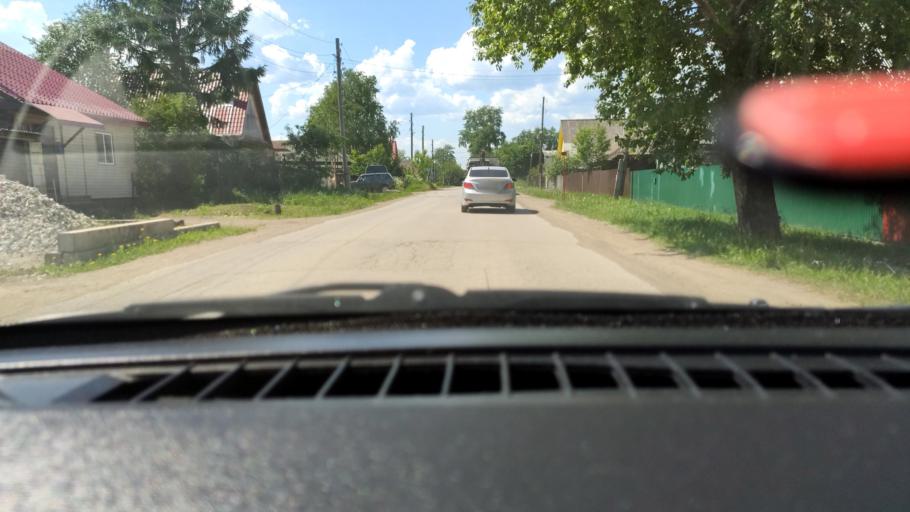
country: RU
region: Perm
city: Sylva
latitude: 58.0331
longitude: 56.7654
